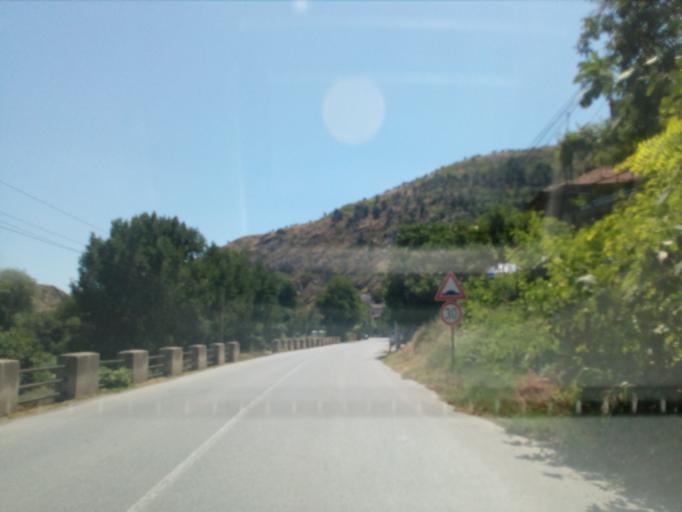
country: MK
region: Veles
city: Veles
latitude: 41.7095
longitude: 21.7846
